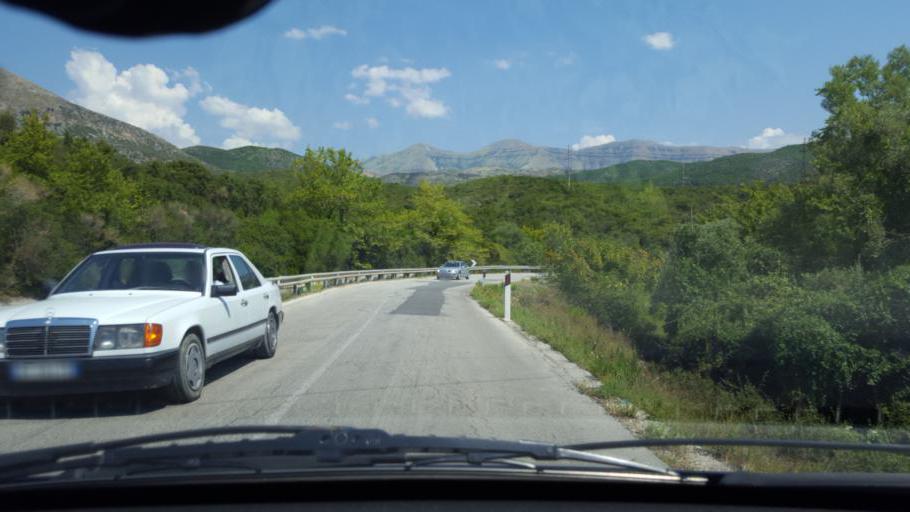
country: AL
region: Vlore
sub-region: Rrethi i Delvines
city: Mesopotam
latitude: 39.9113
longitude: 20.1281
